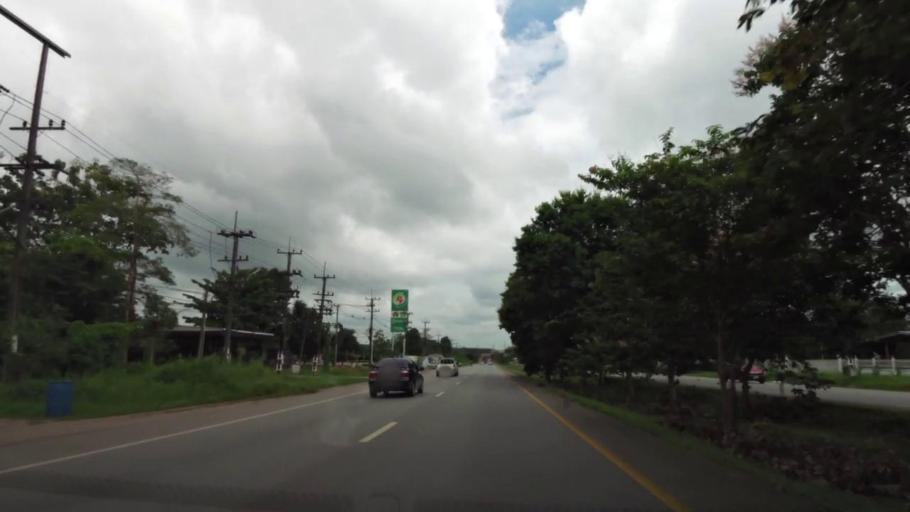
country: TH
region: Chanthaburi
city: Na Yai Am
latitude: 12.7719
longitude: 101.8426
